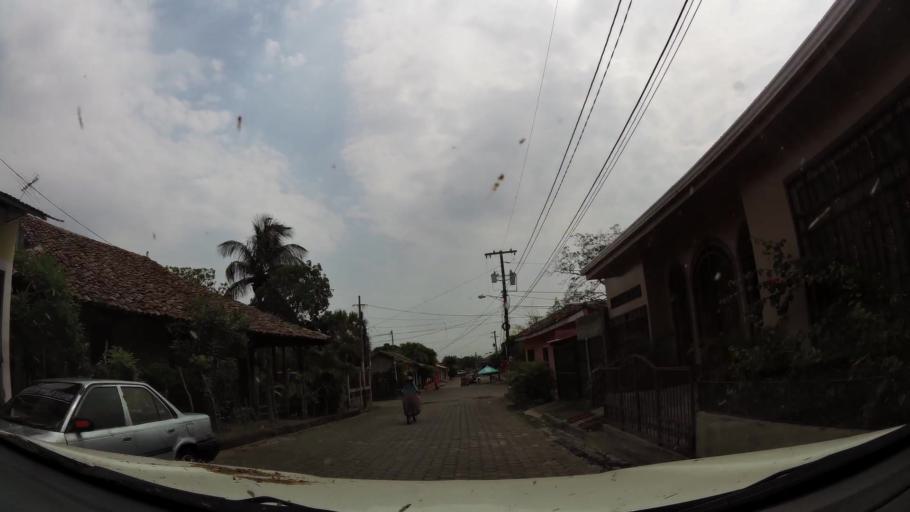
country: NI
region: Granada
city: Diria
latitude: 11.8862
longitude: -86.0551
